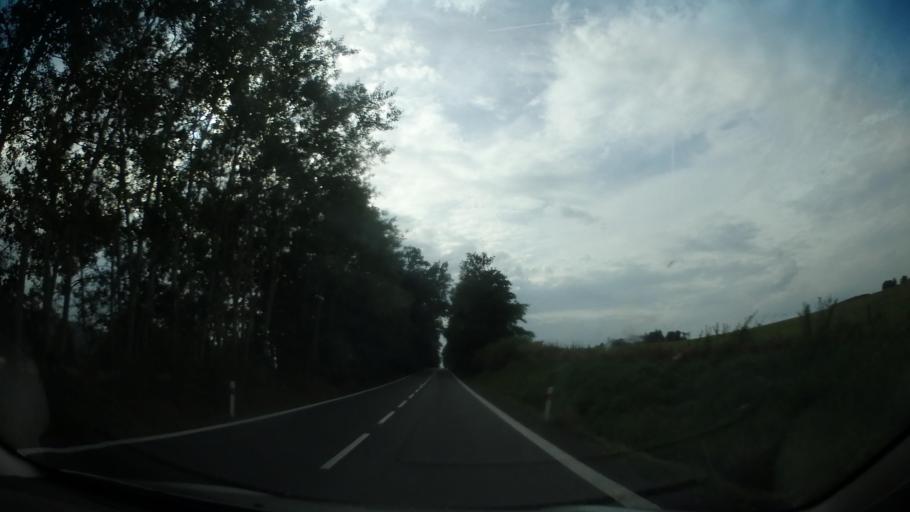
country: CZ
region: Pardubicky
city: Prachovice
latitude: 49.8702
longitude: 15.6216
